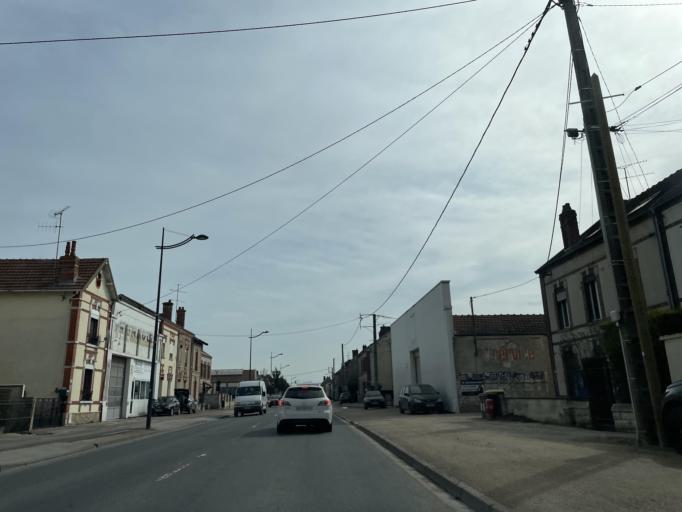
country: FR
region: Champagne-Ardenne
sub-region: Departement de l'Aube
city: Romilly-sur-Seine
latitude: 48.5112
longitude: 3.7223
